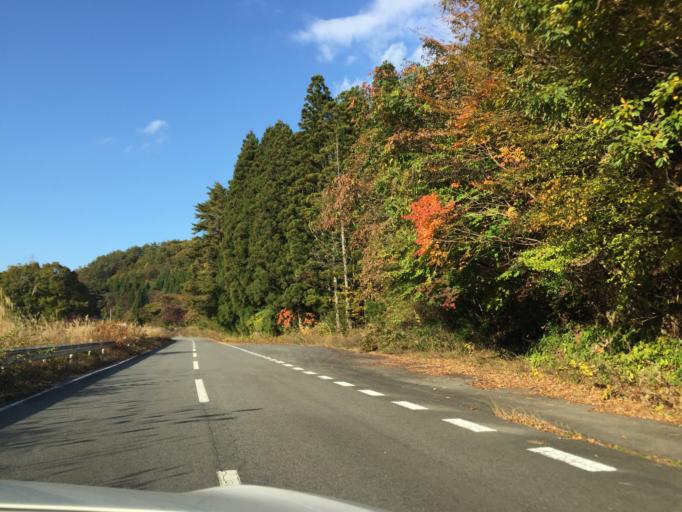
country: JP
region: Fukushima
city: Iwaki
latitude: 37.2474
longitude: 140.7617
